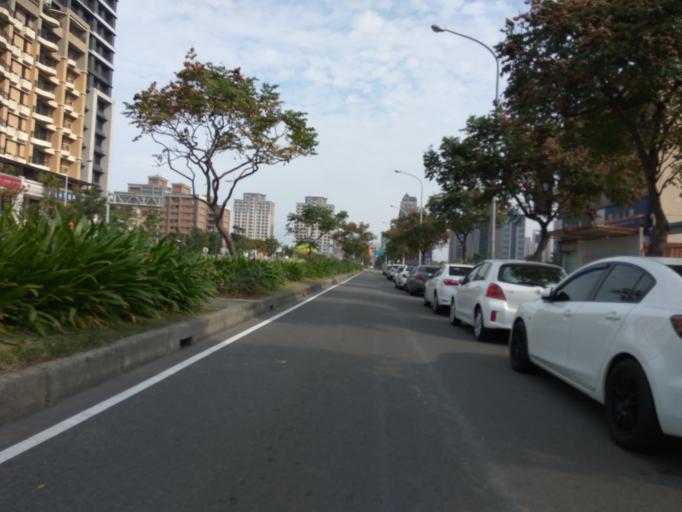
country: TW
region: Taiwan
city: Taoyuan City
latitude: 25.0053
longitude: 121.2151
